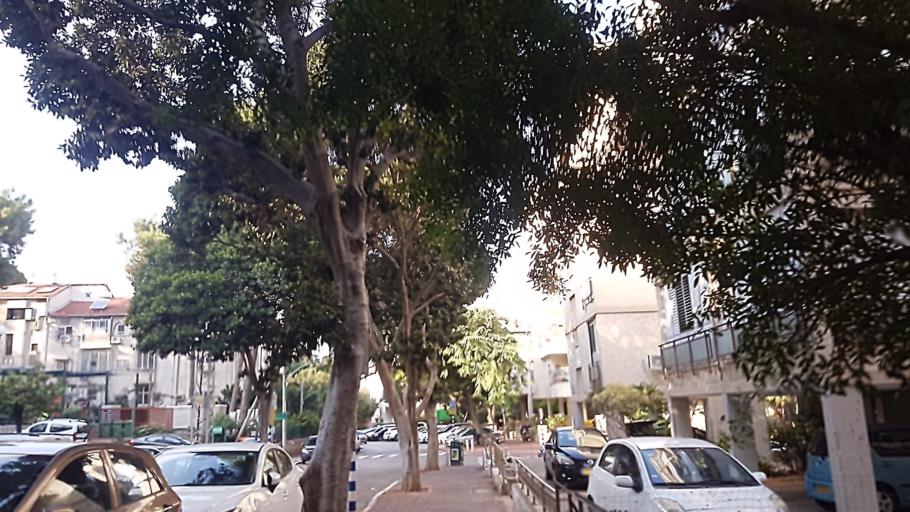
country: IL
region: Tel Aviv
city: Ramat Gan
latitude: 32.0815
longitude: 34.8133
